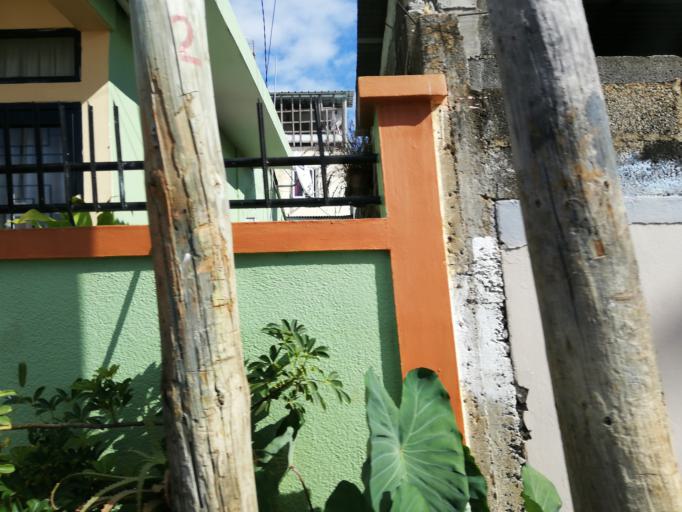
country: MU
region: Black River
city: Petite Riviere
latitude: -20.2226
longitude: 57.4550
